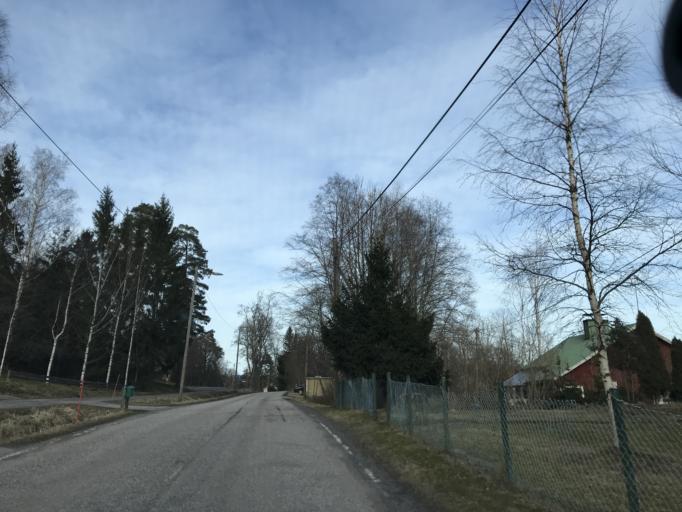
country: FI
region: Uusimaa
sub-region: Raaseporin
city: Pohja
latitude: 60.0924
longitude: 23.5173
